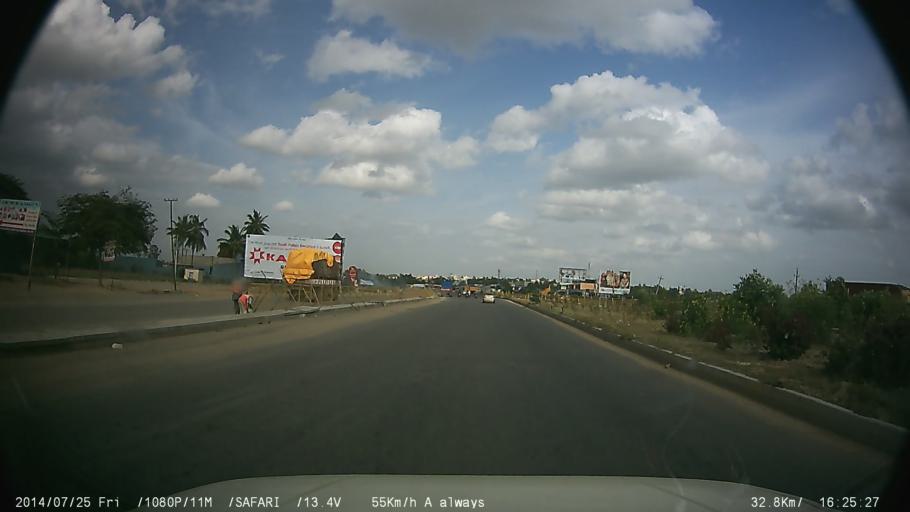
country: IN
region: Tamil Nadu
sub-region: Krishnagiri
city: Hosur
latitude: 12.7750
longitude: 77.7803
